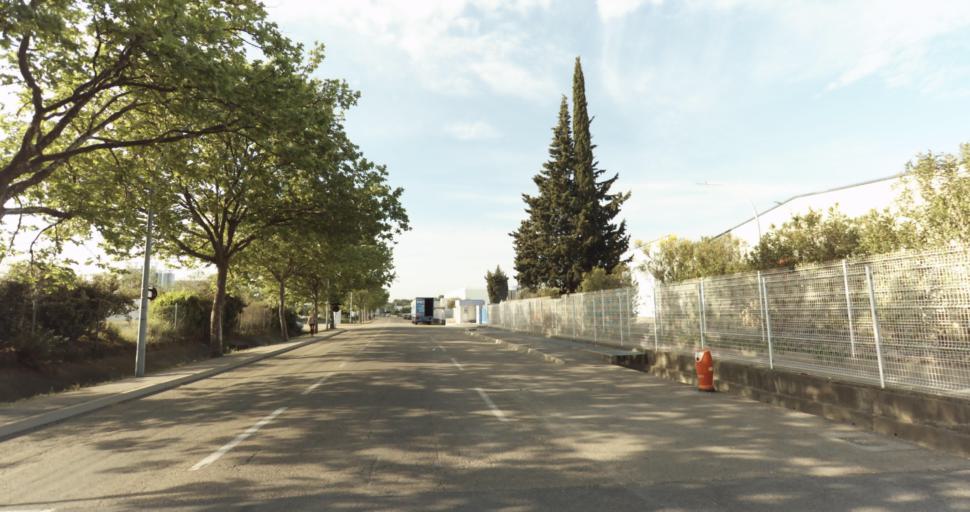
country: FR
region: Languedoc-Roussillon
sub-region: Departement du Gard
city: Rodilhan
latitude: 43.8395
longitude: 4.4167
